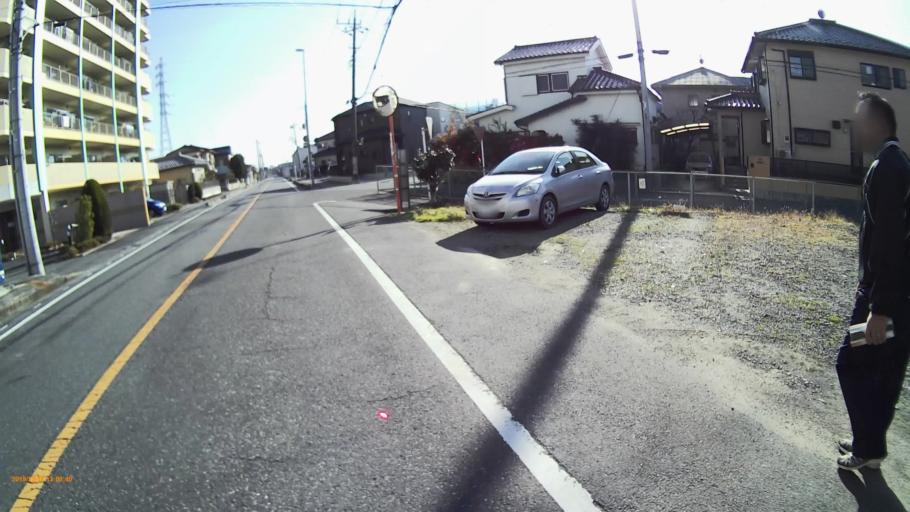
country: JP
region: Saitama
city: Fukiage-fujimi
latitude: 36.0970
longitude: 139.4618
